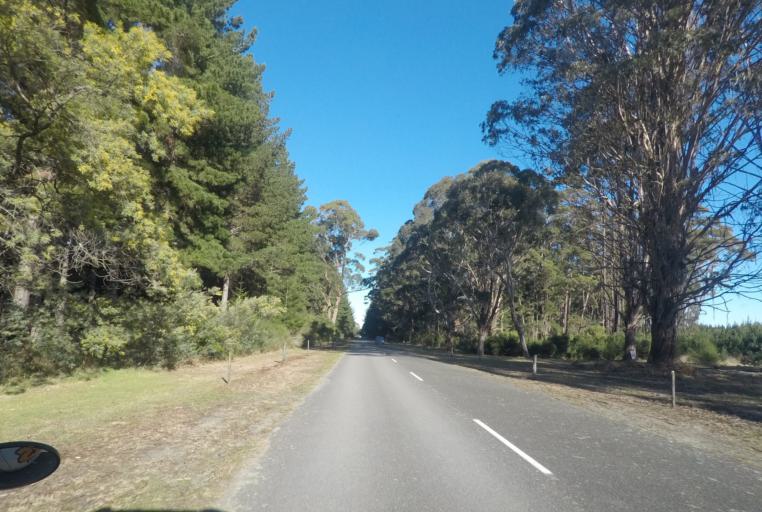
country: NZ
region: Tasman
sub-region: Tasman District
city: Mapua
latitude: -41.2679
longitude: 173.1518
